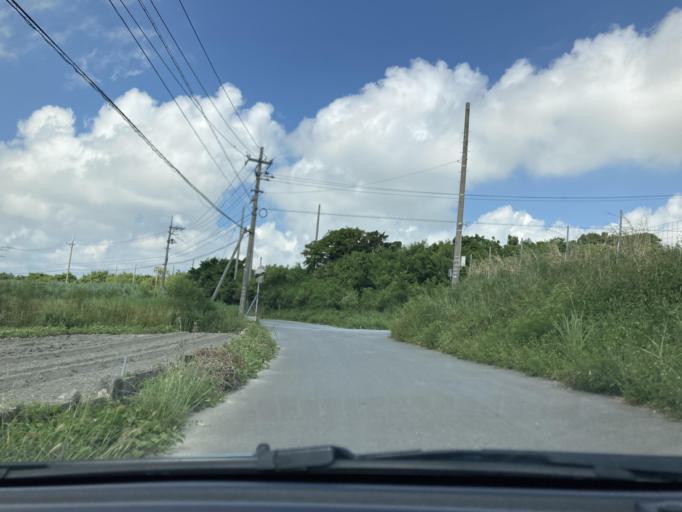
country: JP
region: Okinawa
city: Itoman
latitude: 26.1033
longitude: 127.7259
